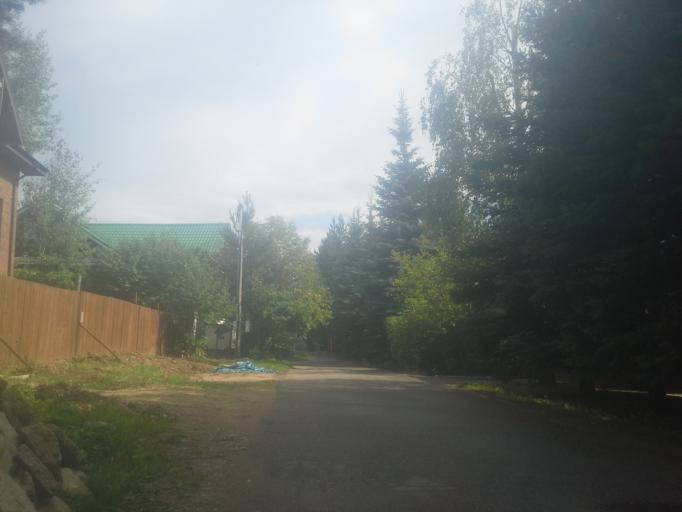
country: RU
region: Moskovskaya
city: Zhavoronki
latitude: 55.6447
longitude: 37.1415
